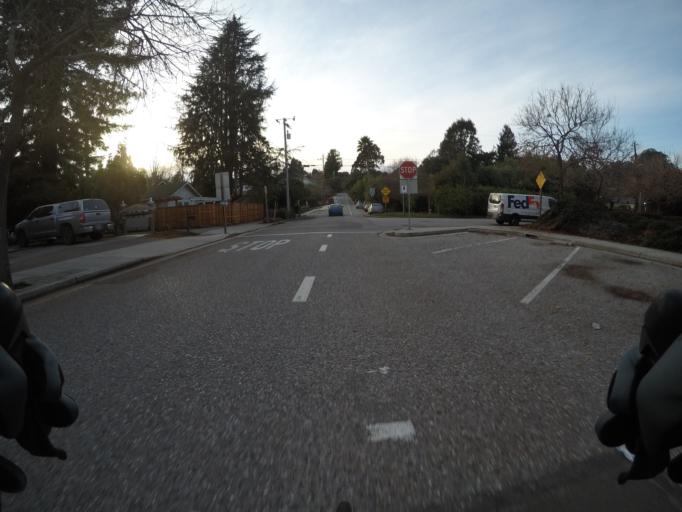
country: US
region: California
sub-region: Santa Cruz County
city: Soquel
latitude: 36.9859
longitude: -121.9581
